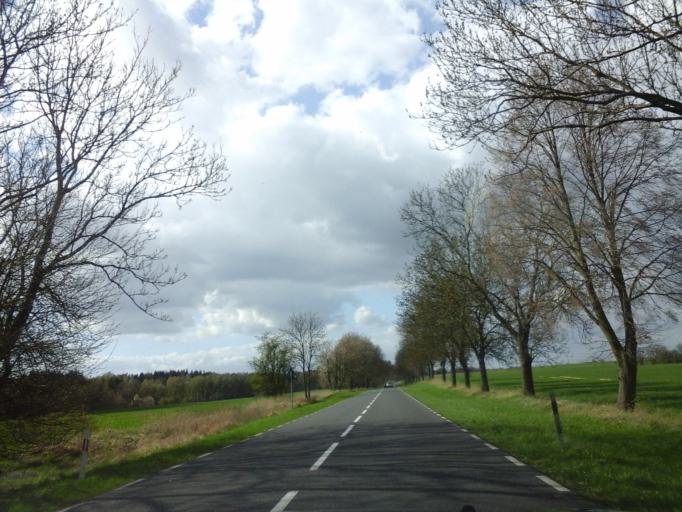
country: PL
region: West Pomeranian Voivodeship
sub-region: Powiat stargardzki
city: Suchan
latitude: 53.2115
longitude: 15.3166
